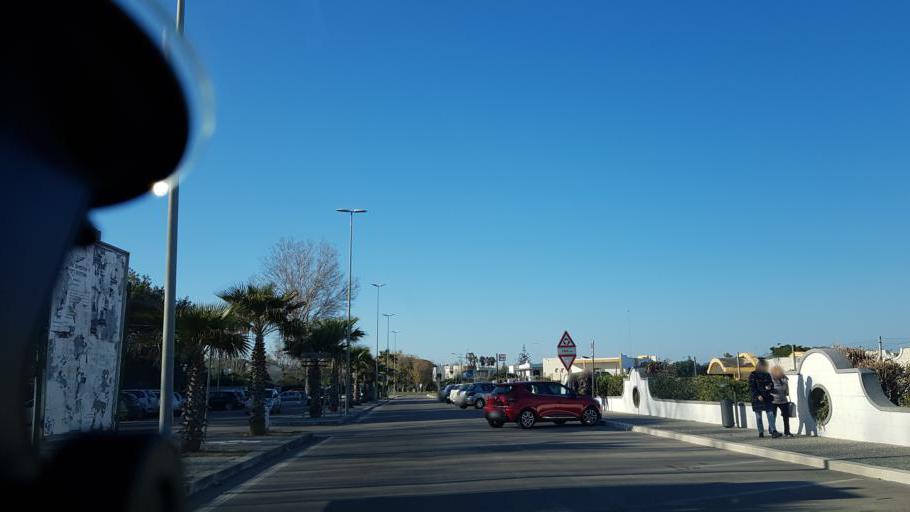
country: IT
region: Apulia
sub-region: Provincia di Lecce
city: Struda
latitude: 40.3863
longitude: 18.3043
